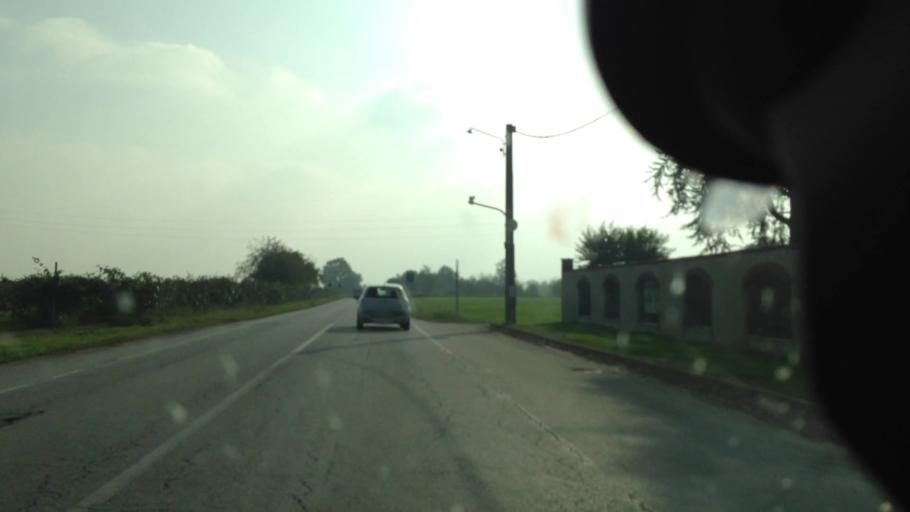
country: IT
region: Piedmont
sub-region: Provincia di Vercelli
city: Borgo d'Ale
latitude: 45.3392
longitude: 8.0453
